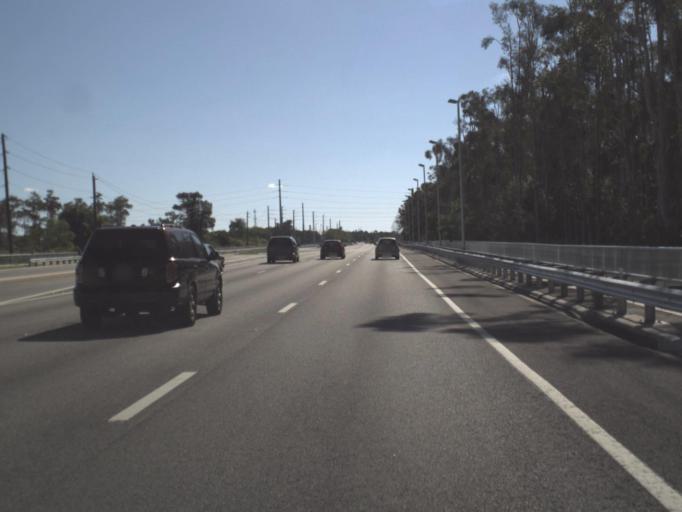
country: US
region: Florida
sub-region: Lee County
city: Tice
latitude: 26.6304
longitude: -81.7884
